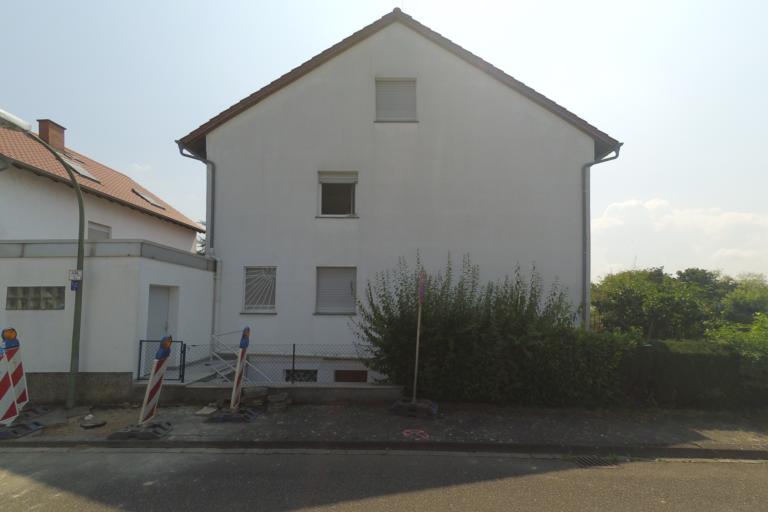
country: DE
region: Rheinland-Pfalz
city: Mutterstadt
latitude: 49.4582
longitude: 8.3703
